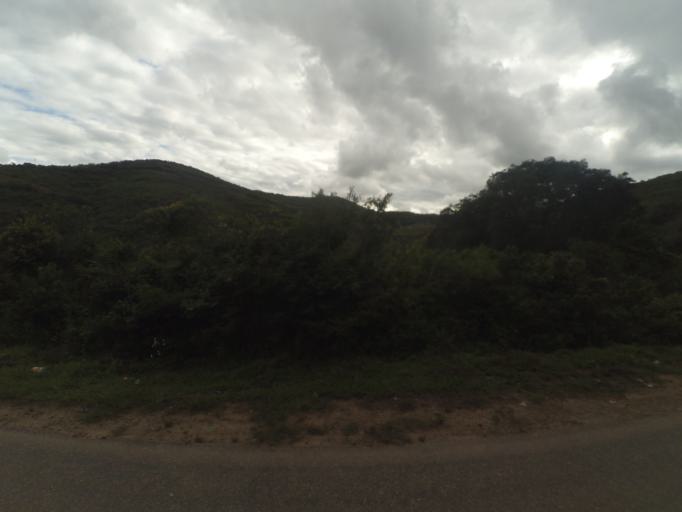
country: BO
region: Santa Cruz
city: Samaipata
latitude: -18.1725
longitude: -63.8443
